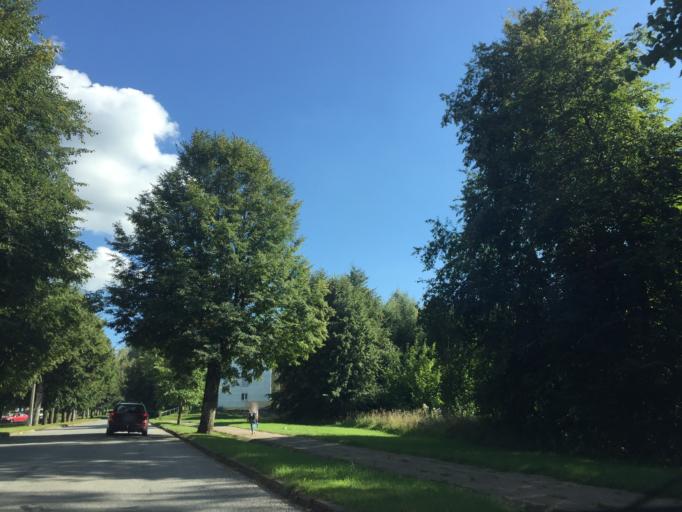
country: LV
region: Priekuli
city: Priekuli
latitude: 57.3859
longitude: 25.4234
